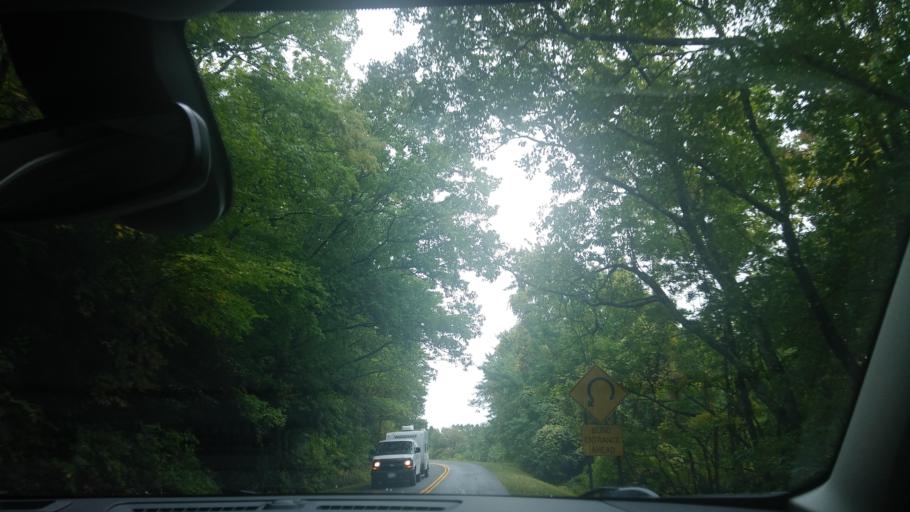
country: US
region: North Carolina
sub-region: Mitchell County
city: Spruce Pine
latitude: 35.9060
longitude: -81.9696
